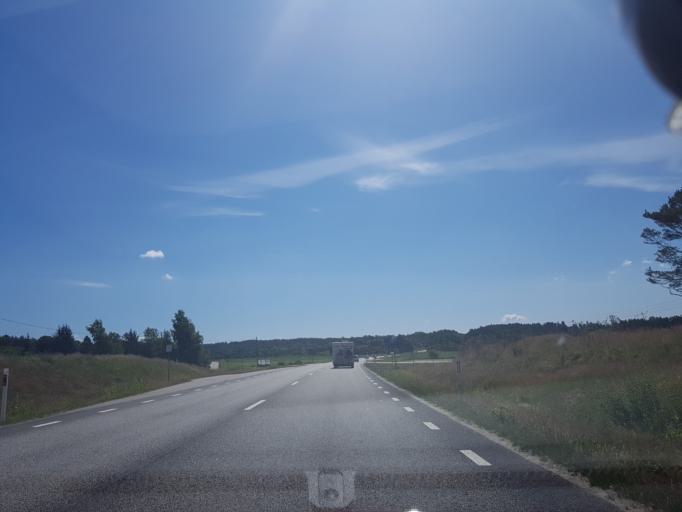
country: SE
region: Vaestra Goetaland
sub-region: Orust
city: Henan
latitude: 58.1440
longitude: 11.6379
